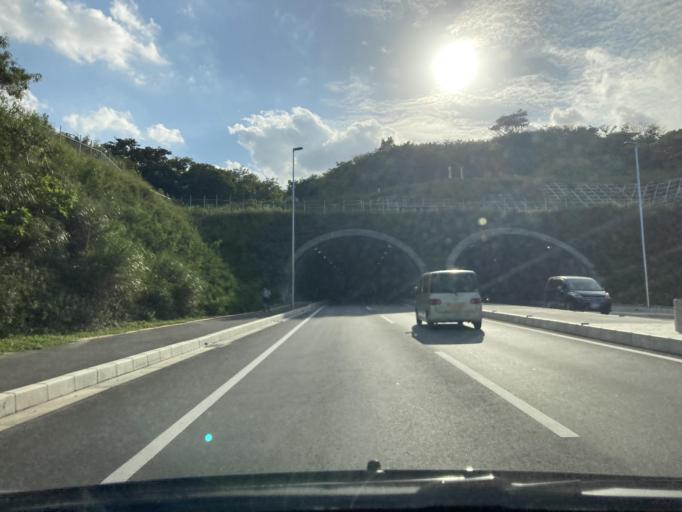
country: JP
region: Okinawa
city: Chatan
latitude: 26.2997
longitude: 127.8034
